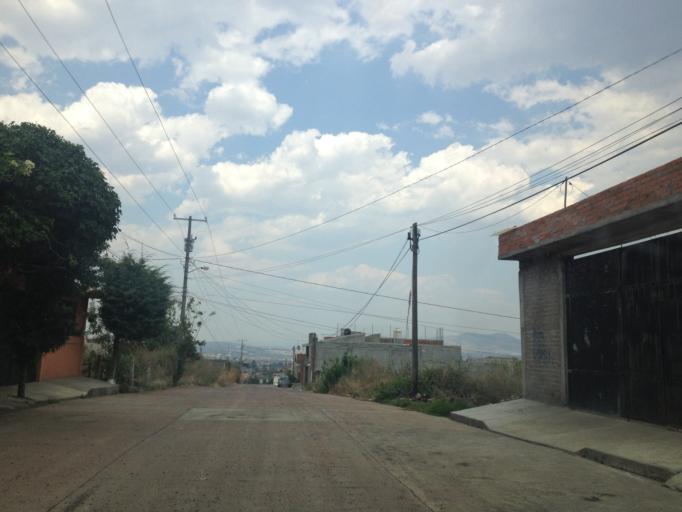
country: MX
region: Michoacan
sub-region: Morelia
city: San Antonio
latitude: 19.7084
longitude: -101.2476
